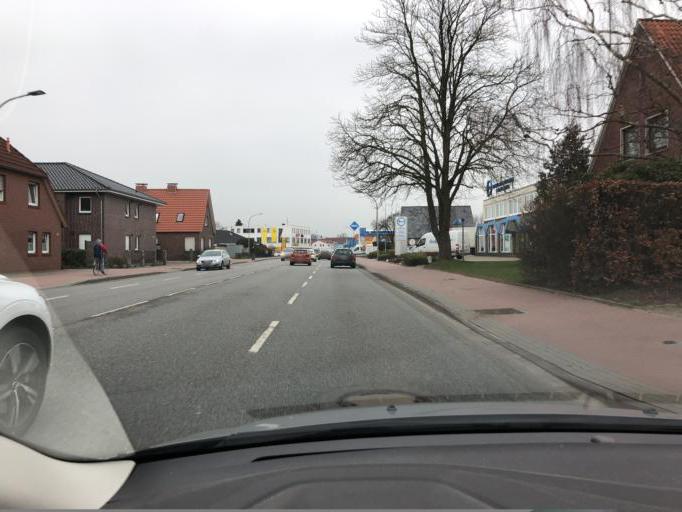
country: DE
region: Lower Saxony
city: Aurich
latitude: 53.4637
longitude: 7.4885
